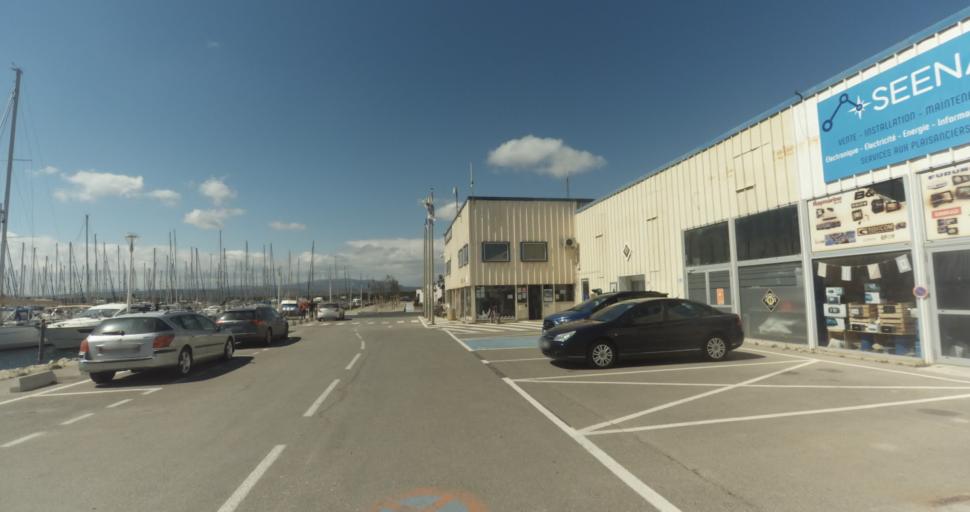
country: FR
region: Languedoc-Roussillon
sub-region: Departement de l'Aude
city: Leucate
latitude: 42.8661
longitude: 3.0422
